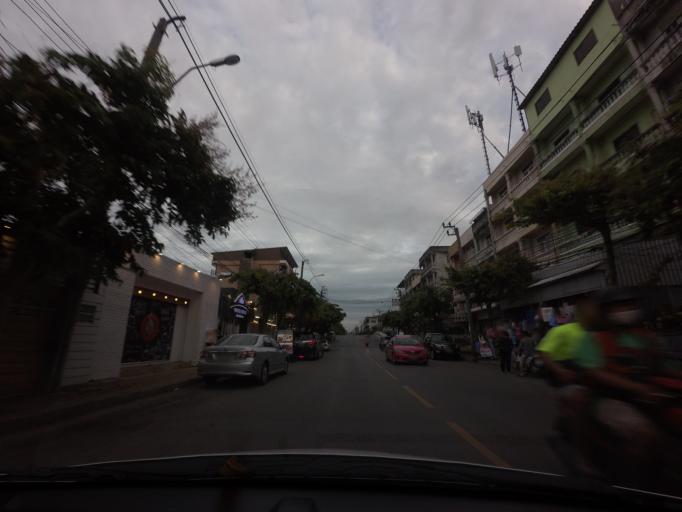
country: TH
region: Bangkok
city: Chom Thong
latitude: 13.6864
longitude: 100.4635
